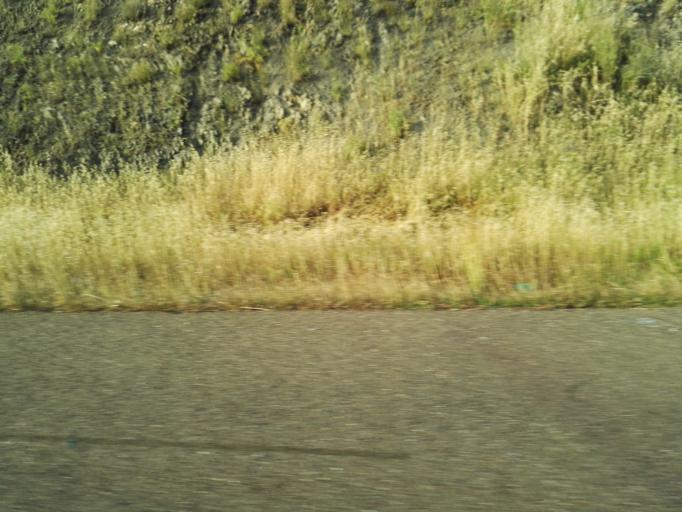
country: PT
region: Portalegre
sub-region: Elvas
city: Elvas
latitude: 38.8937
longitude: -7.1192
